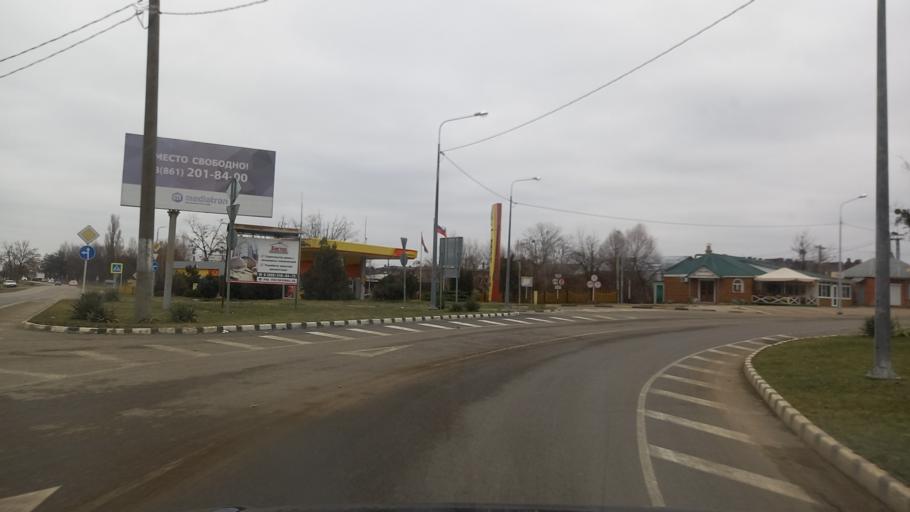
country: RU
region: Krasnodarskiy
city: Goryachiy Klyuch
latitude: 44.6491
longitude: 39.1698
